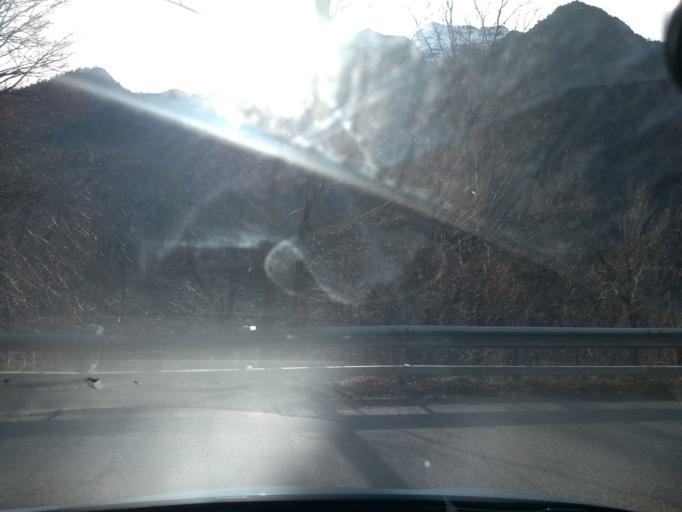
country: IT
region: Piedmont
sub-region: Provincia di Torino
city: Ala di Stura
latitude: 45.3147
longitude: 7.2833
